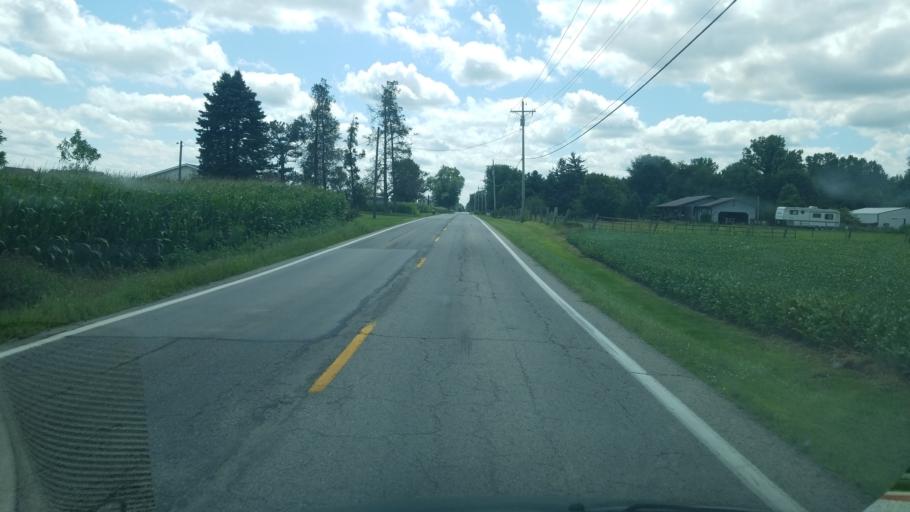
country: US
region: Ohio
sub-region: Henry County
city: Liberty Center
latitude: 41.4790
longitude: -84.0088
